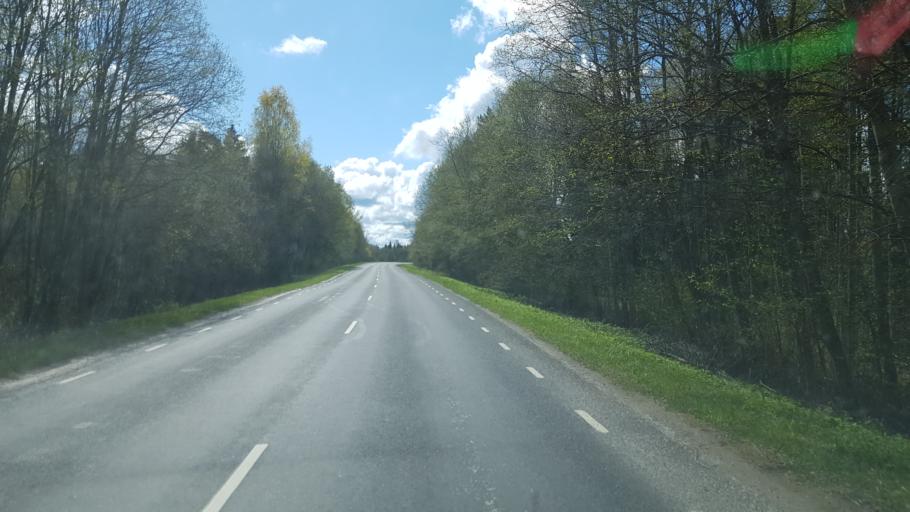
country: EE
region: Harju
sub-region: Raasiku vald
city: Raasiku
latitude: 59.1480
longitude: 25.1988
